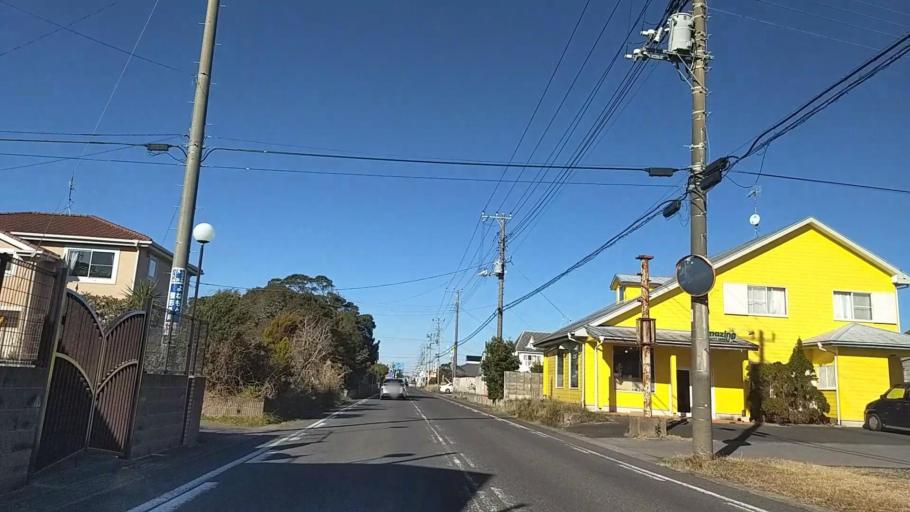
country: JP
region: Chiba
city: Mobara
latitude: 35.3708
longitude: 140.3876
